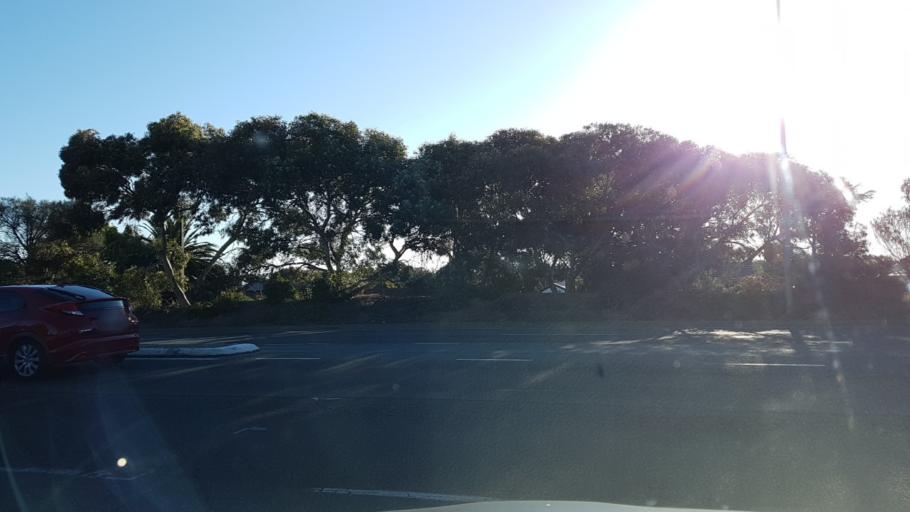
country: AU
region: South Australia
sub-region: Onkaparinga
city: Bedford Park
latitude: -35.0425
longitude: 138.5702
